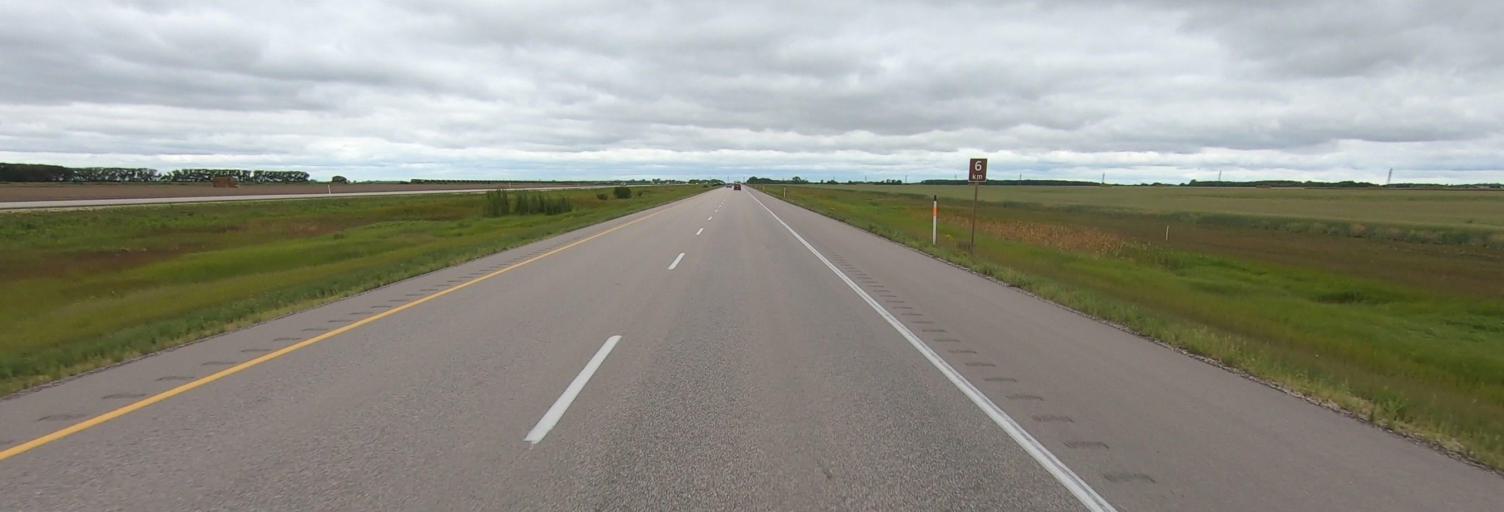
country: CA
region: Manitoba
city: Portage la Prairie
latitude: 49.9249
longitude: -97.8538
